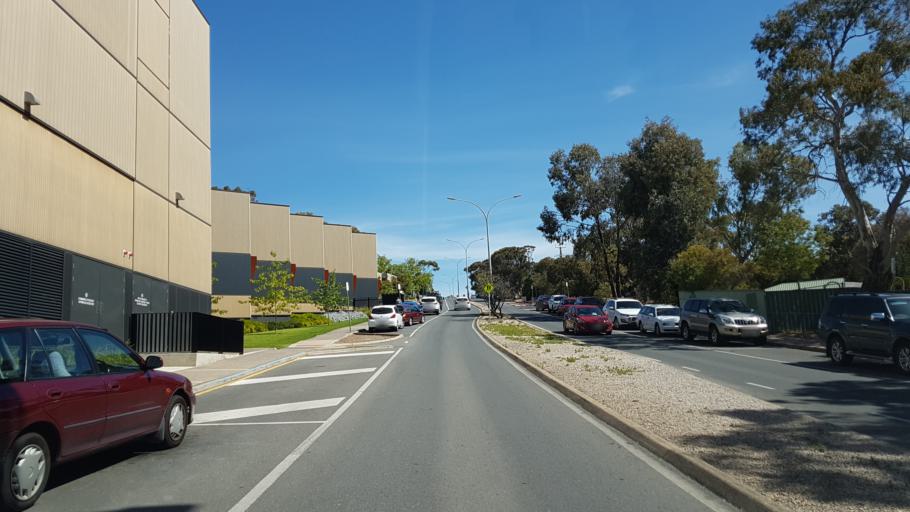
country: AU
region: South Australia
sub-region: Marion
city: Marion
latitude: -35.0235
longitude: 138.5679
